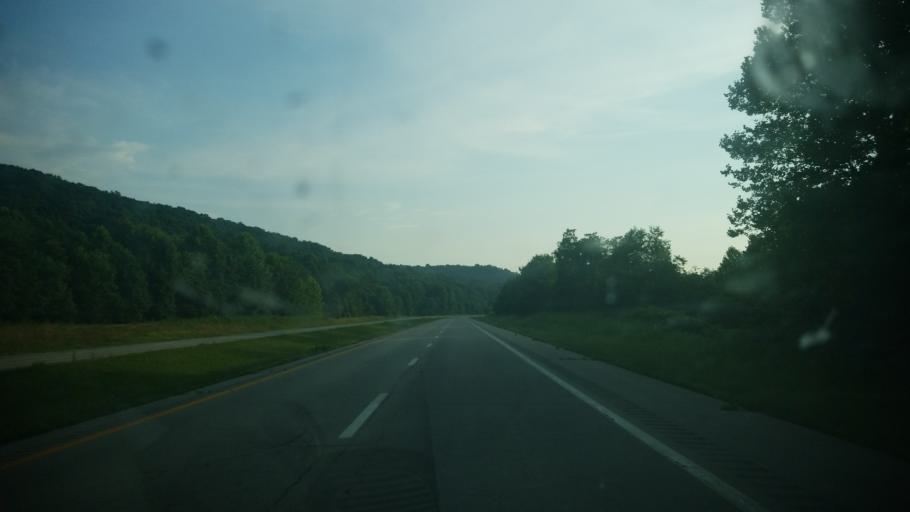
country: US
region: Ohio
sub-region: Pike County
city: Piketon
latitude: 39.0470
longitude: -83.2148
